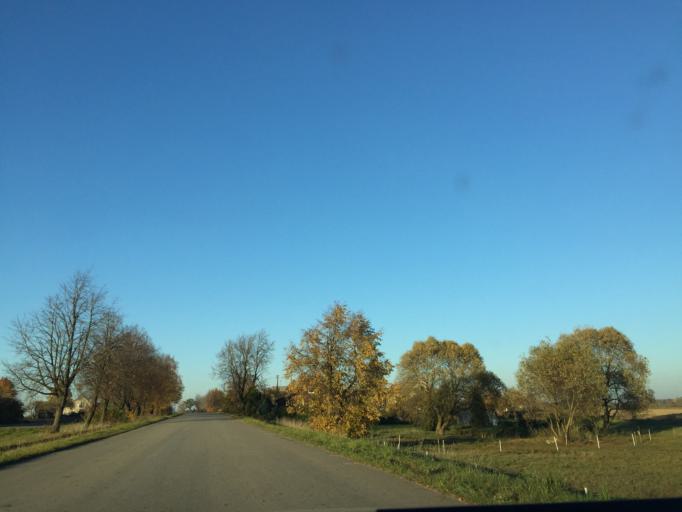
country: LT
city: Vieksniai
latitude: 56.2498
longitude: 22.5213
